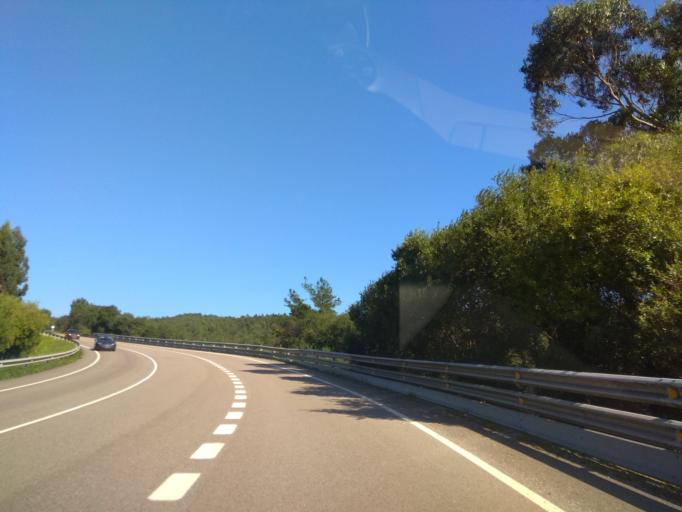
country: ES
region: Cantabria
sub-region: Provincia de Cantabria
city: Bareyo
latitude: 43.4705
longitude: -3.6460
